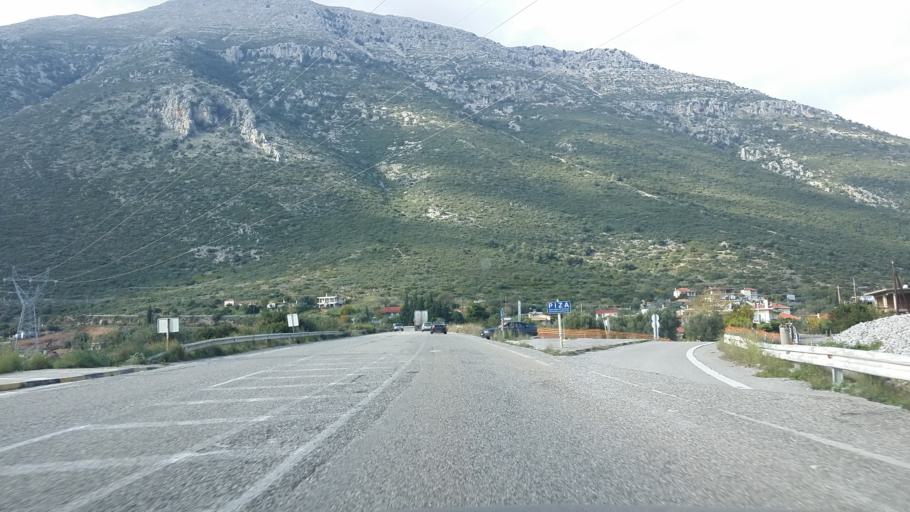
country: GR
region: West Greece
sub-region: Nomos Aitolias kai Akarnanias
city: Antirrio
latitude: 38.3545
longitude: 21.7058
